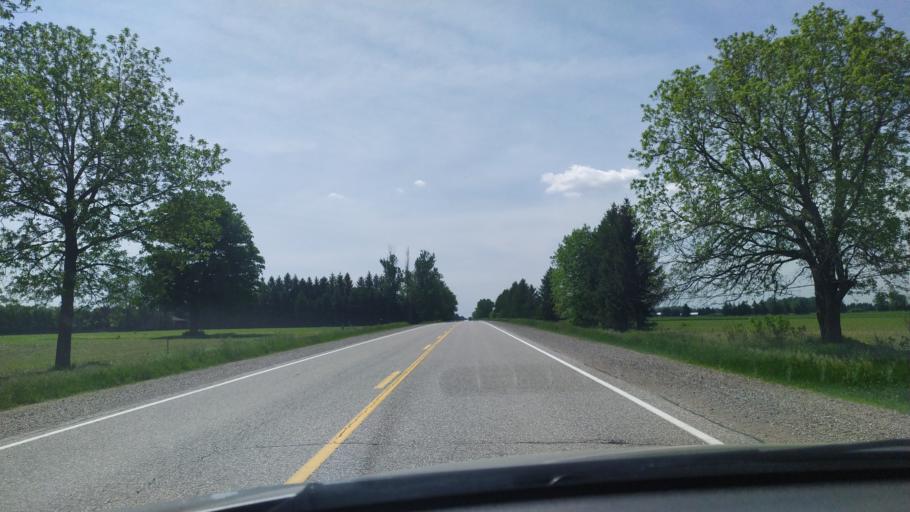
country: CA
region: Ontario
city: Dorchester
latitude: 43.1227
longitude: -81.0219
